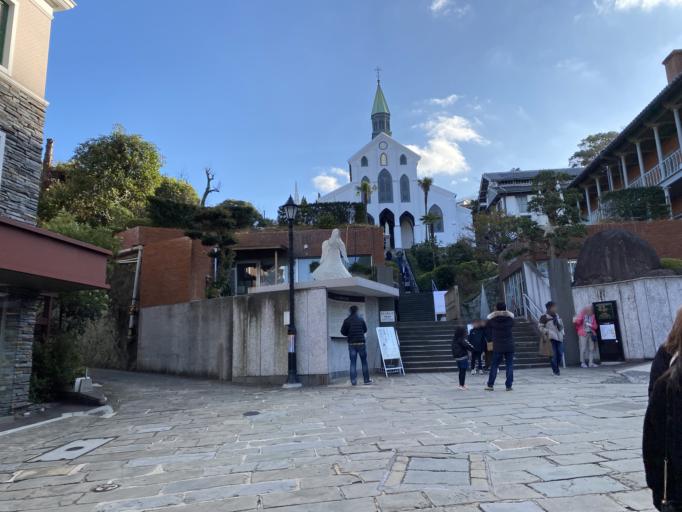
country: JP
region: Nagasaki
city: Nagasaki-shi
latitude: 32.7348
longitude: 129.8701
